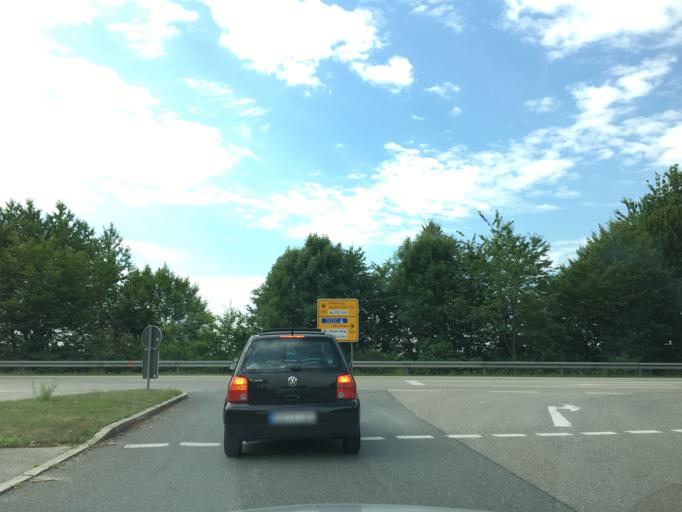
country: DE
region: Bavaria
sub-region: Upper Bavaria
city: Erding
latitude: 48.2832
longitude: 11.8955
